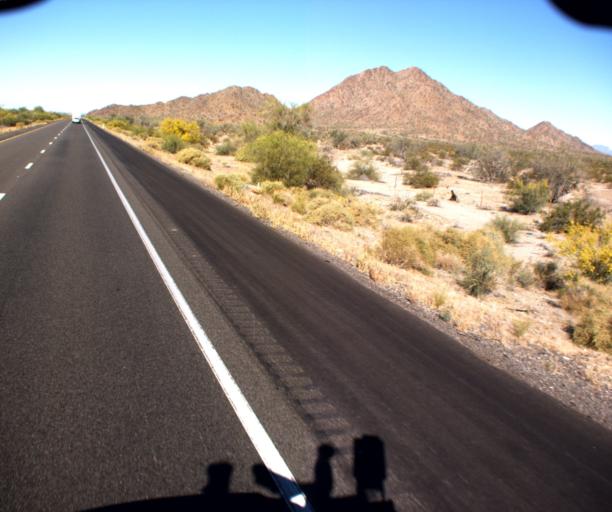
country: US
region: Arizona
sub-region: Maricopa County
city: Gila Bend
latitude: 32.9075
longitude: -112.5467
